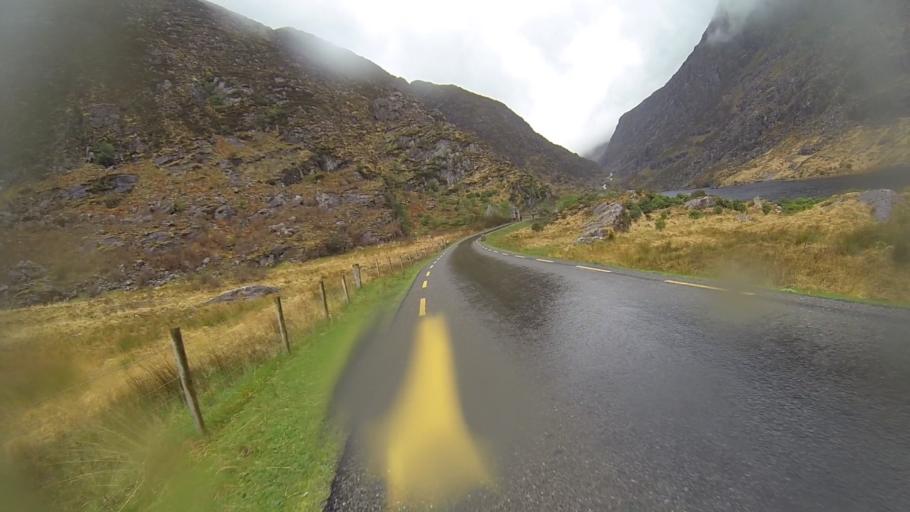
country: IE
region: Munster
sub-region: Ciarrai
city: Cill Airne
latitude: 52.0149
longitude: -9.6353
